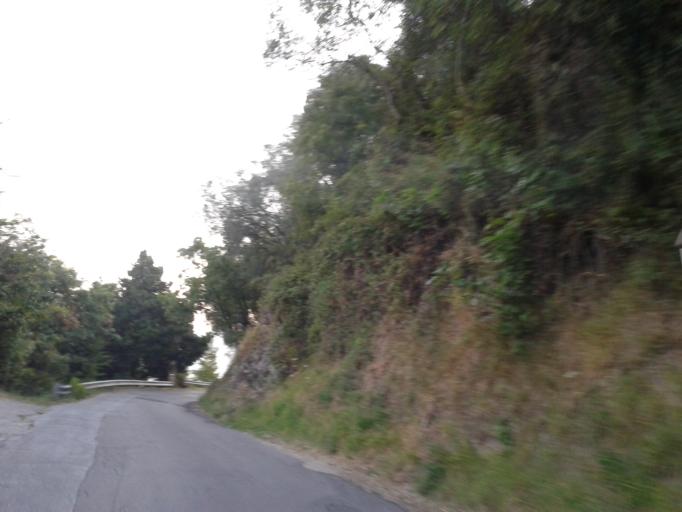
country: IT
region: Tuscany
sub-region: Provincia di Lucca
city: Pontestazzemese
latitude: 43.9608
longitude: 10.3266
